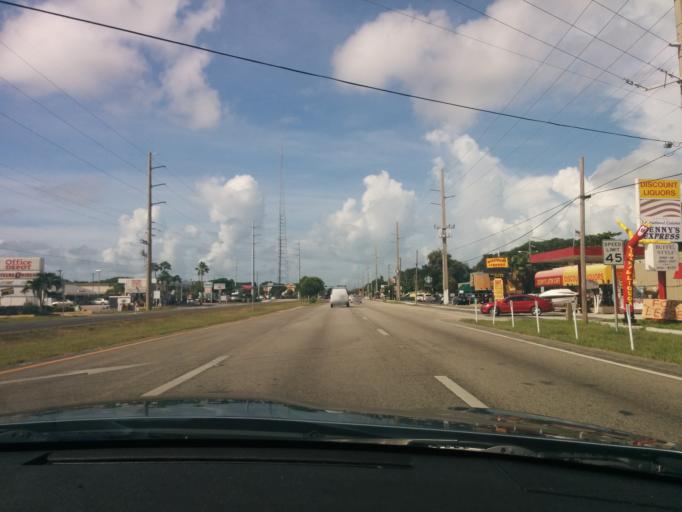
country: US
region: Florida
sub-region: Monroe County
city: Key Largo
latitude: 25.0955
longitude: -80.4398
